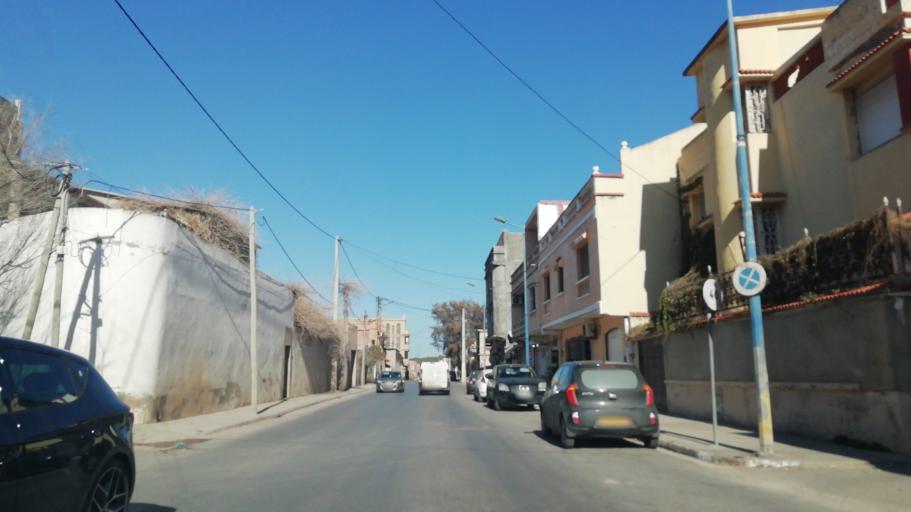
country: DZ
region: Oran
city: Bir el Djir
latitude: 35.7486
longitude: -0.5678
